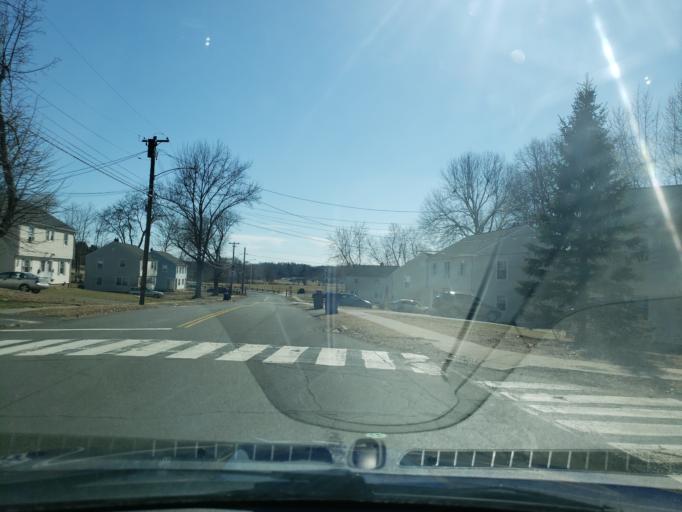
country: US
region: Connecticut
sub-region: Hartford County
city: Enfield
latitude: 41.9815
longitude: -72.5988
